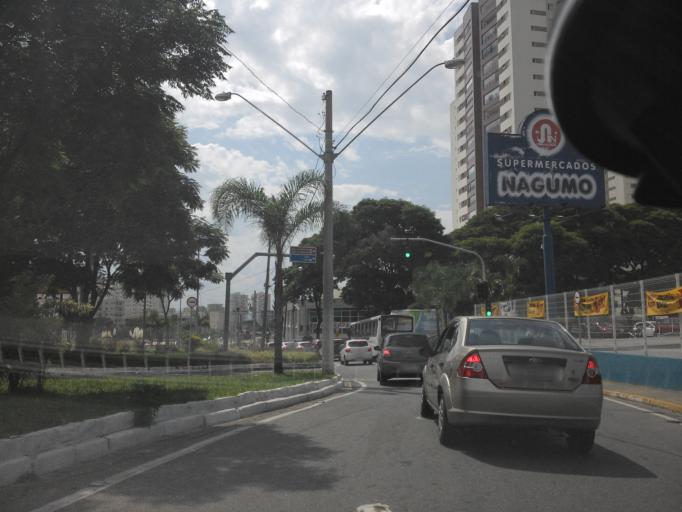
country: BR
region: Sao Paulo
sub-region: Taubate
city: Taubate
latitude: -23.0252
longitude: -45.5709
